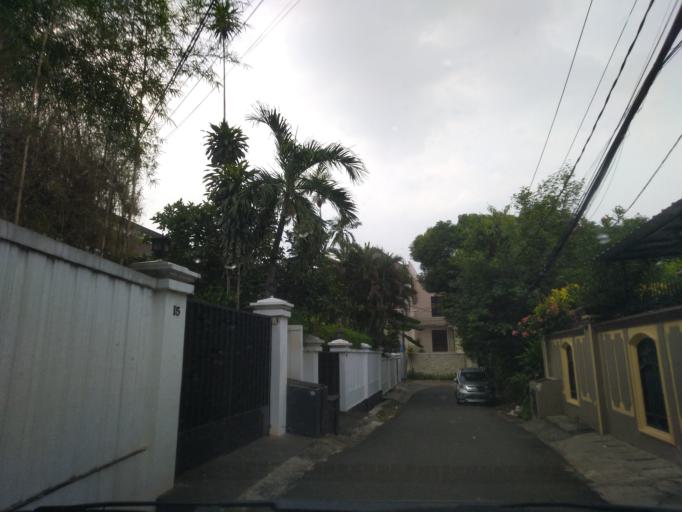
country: ID
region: Jakarta Raya
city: Jakarta
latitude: -6.2615
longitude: 106.8198
